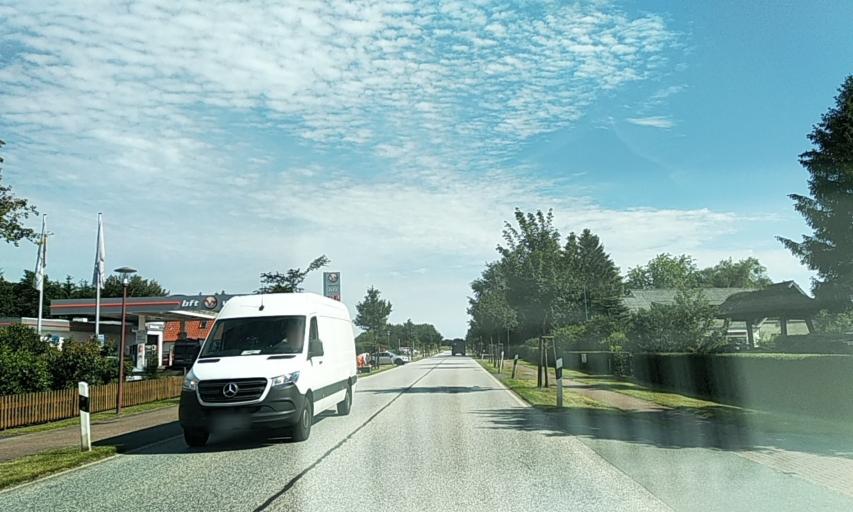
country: DE
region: Schleswig-Holstein
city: Jagel
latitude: 54.4590
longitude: 9.5383
